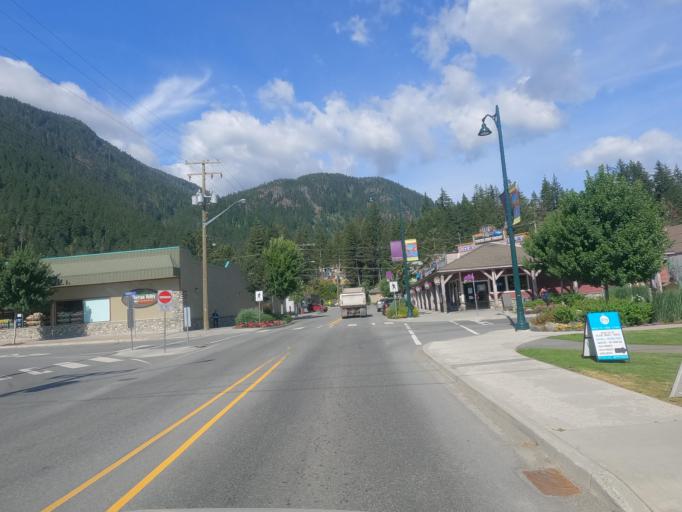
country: CA
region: British Columbia
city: Pemberton
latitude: 50.3222
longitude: -122.8060
